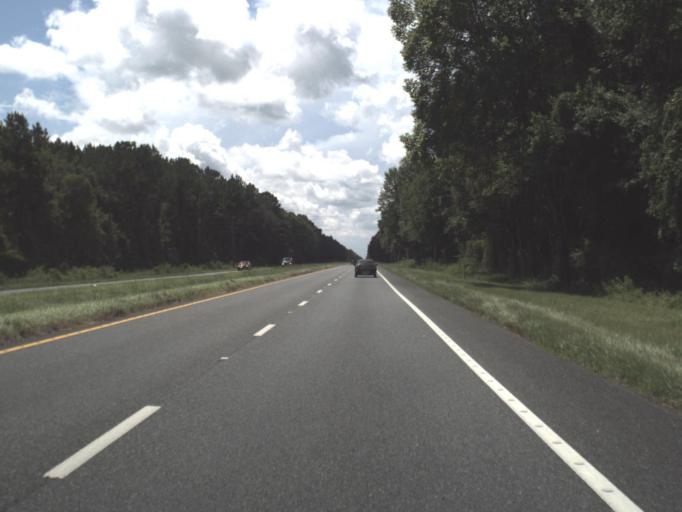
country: US
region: Florida
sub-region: Taylor County
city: Perry
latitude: 30.2616
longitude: -83.7105
